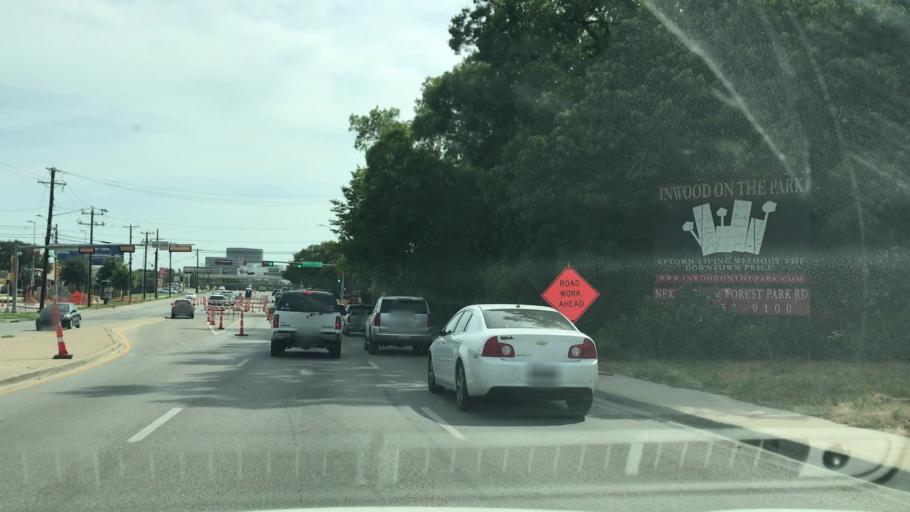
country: US
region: Texas
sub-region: Dallas County
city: Dallas
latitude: 32.8194
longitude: -96.8387
